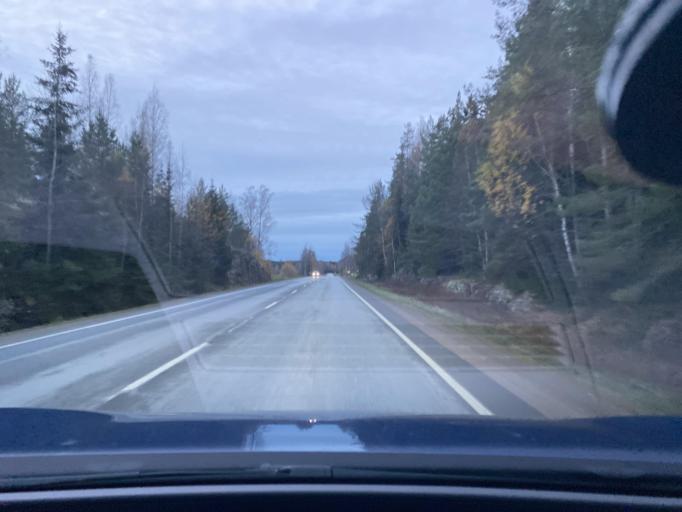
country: FI
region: Uusimaa
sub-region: Helsinki
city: Sammatti
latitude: 60.3871
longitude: 23.8326
